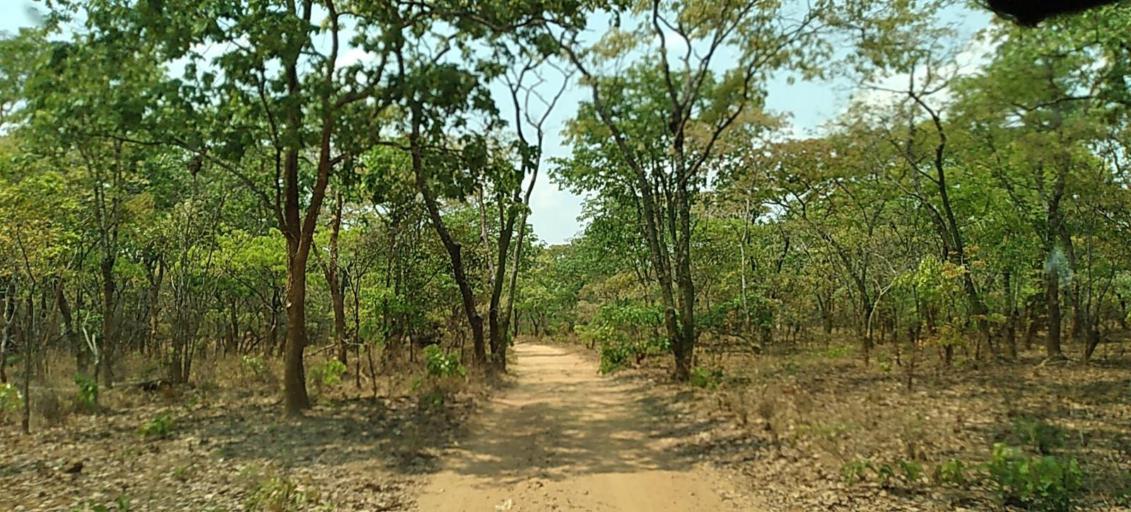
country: ZM
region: North-Western
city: Kabompo
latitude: -13.6505
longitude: 24.3746
